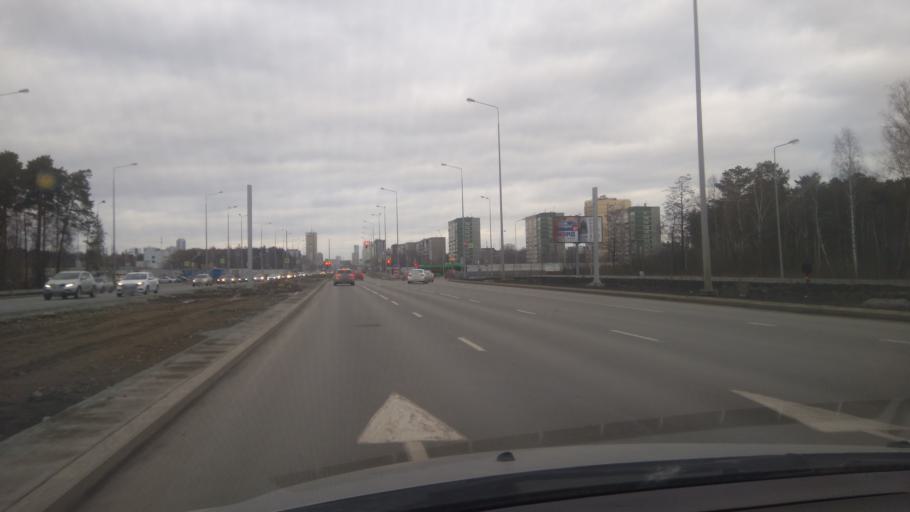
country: RU
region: Sverdlovsk
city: Sovkhoznyy
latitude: 56.8021
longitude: 60.5366
